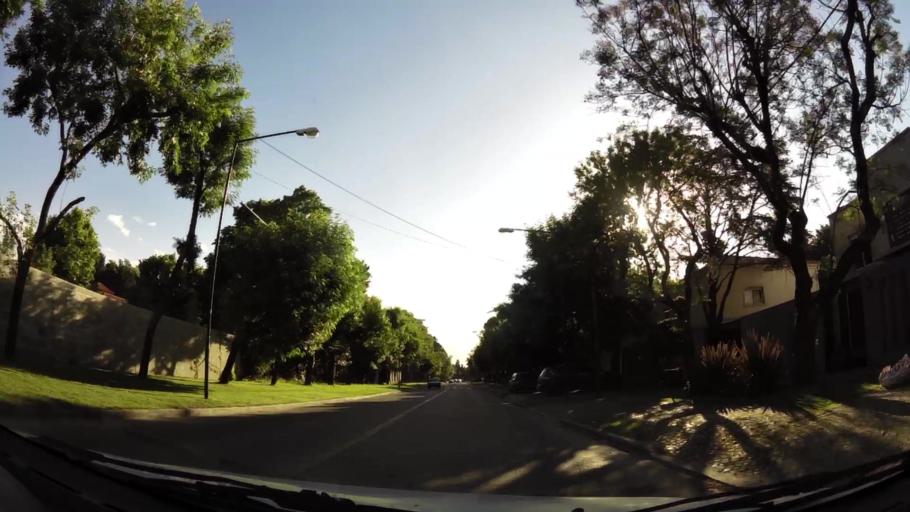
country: AR
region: Buenos Aires
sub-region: Partido de San Isidro
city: San Isidro
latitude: -34.4856
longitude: -58.5455
